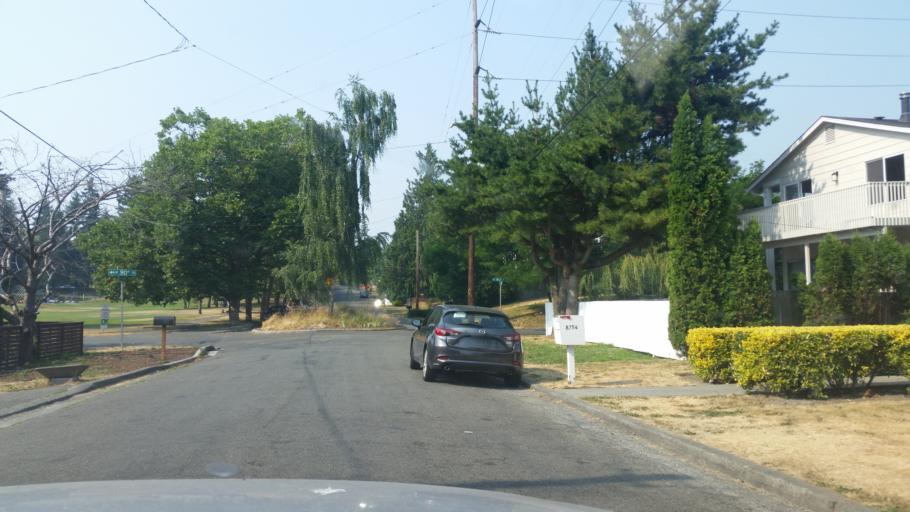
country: US
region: Washington
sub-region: King County
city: Shoreline
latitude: 47.6939
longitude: -122.3580
